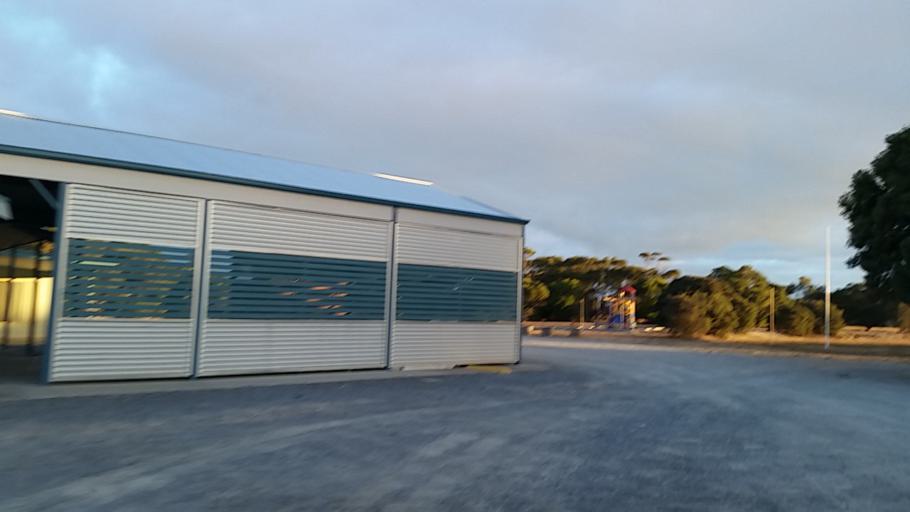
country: AU
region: South Australia
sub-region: Yankalilla
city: Normanville
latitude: -35.6058
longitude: 138.1090
